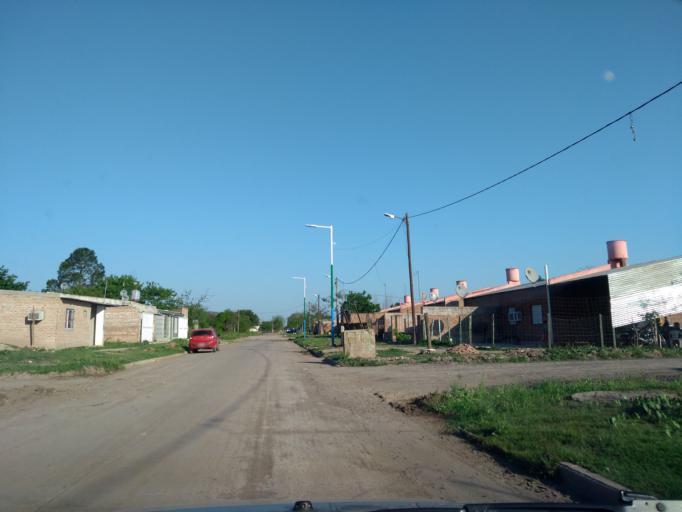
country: AR
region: Chaco
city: Fontana
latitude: -27.4141
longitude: -59.0534
